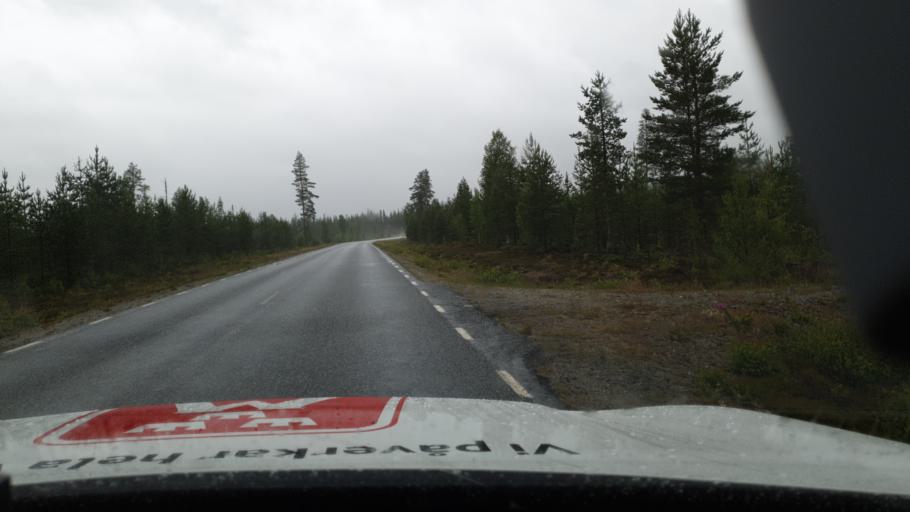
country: SE
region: Vaesterbotten
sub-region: Asele Kommun
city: Asele
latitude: 64.2344
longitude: 17.2966
